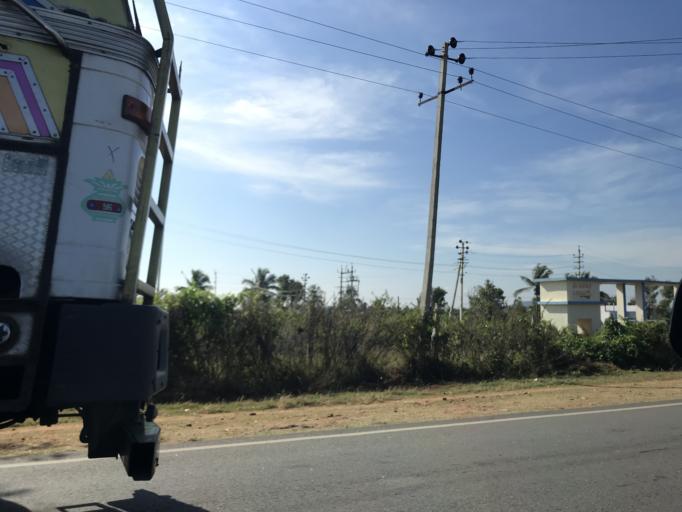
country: IN
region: Karnataka
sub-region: Mysore
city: Mysore
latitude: 12.1998
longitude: 76.5508
